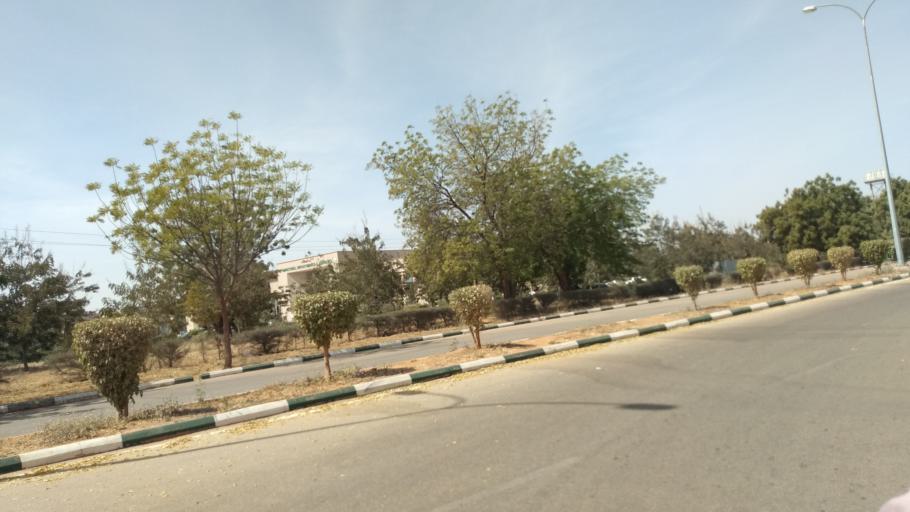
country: NG
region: Jigawa
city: Dutse
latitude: 11.6842
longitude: 9.3334
